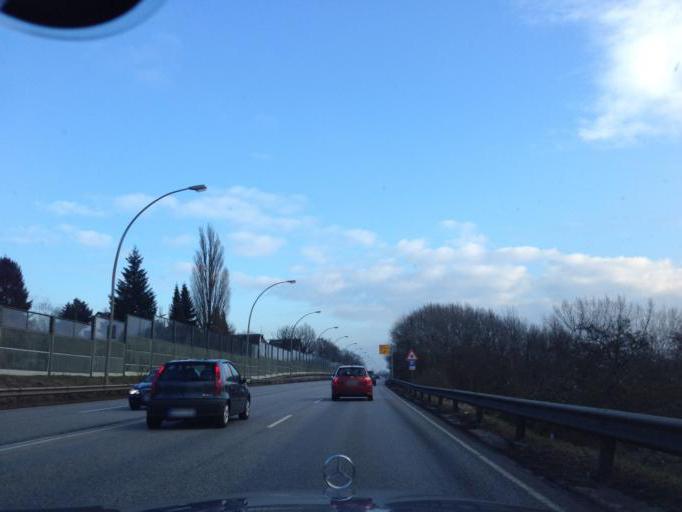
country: DE
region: Schleswig-Holstein
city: Oststeinbek
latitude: 53.5253
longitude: 10.1391
